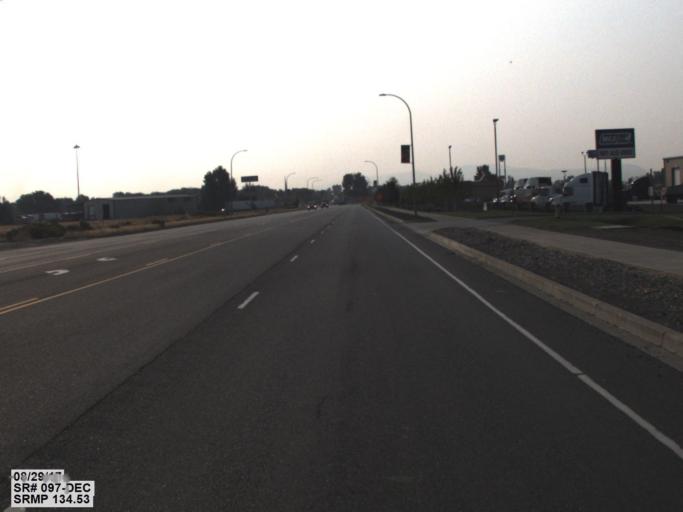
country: US
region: Washington
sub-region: Kittitas County
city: Ellensburg
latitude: 47.0105
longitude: -120.5913
